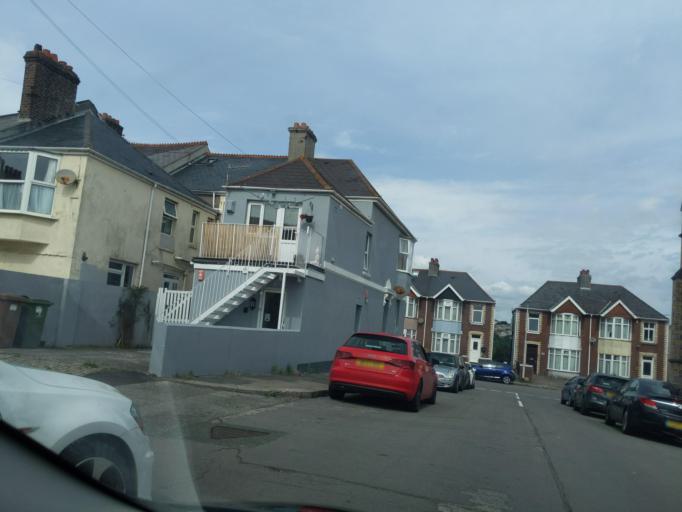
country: GB
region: England
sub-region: Plymouth
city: Plymouth
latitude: 50.3788
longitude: -4.1179
